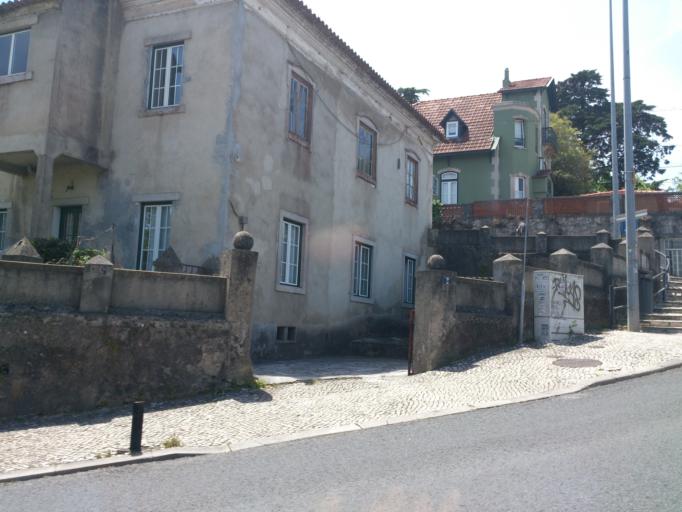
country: PT
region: Lisbon
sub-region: Sintra
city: Sintra
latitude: 38.8006
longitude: -9.3822
